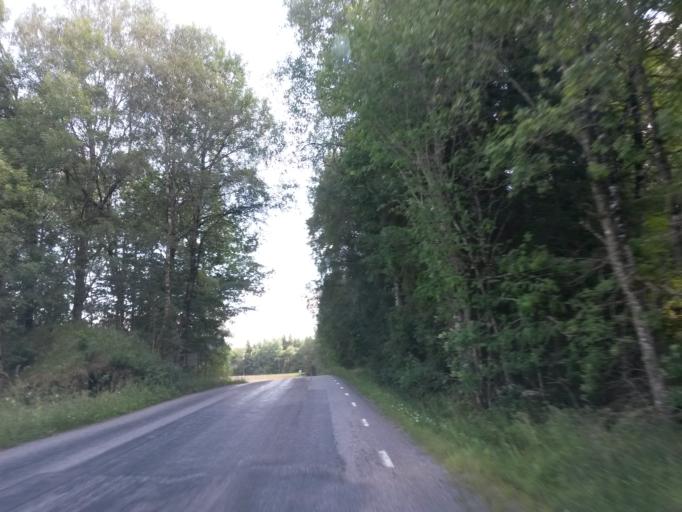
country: SE
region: Vaestra Goetaland
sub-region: Vargarda Kommun
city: Vargarda
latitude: 58.1038
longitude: 12.8119
